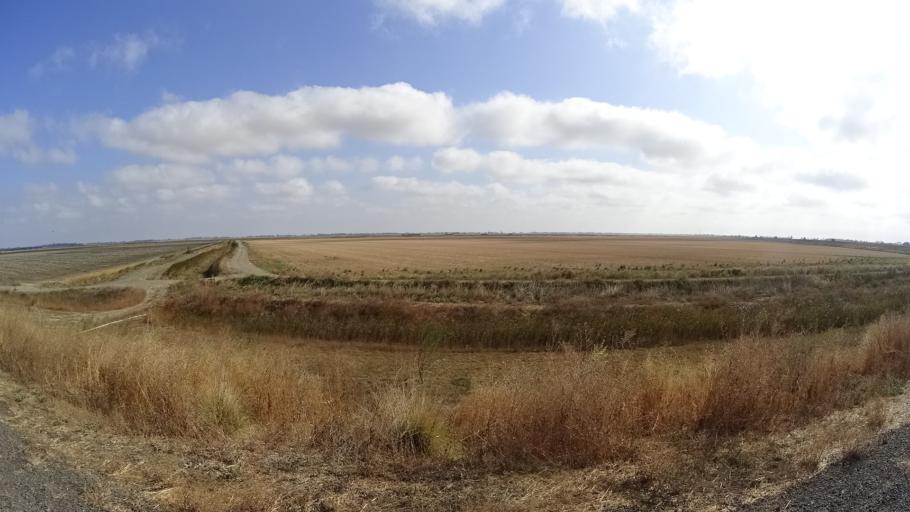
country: US
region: California
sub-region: Yolo County
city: Woodland
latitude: 38.8250
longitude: -121.7961
